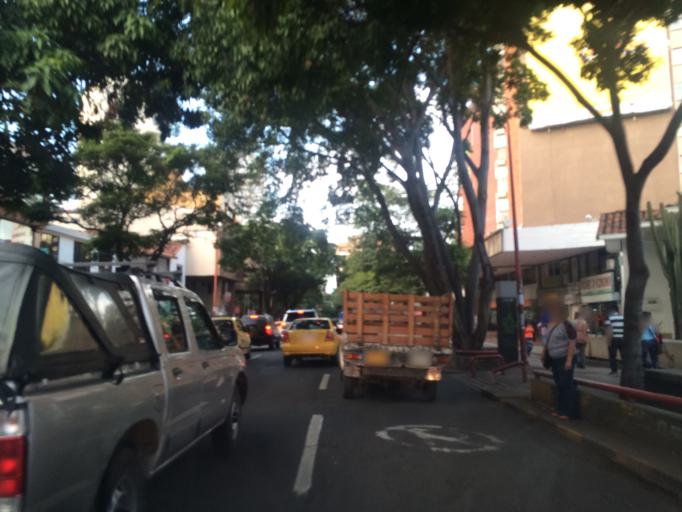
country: CO
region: Valle del Cauca
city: Cali
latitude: 3.4604
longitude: -76.5315
